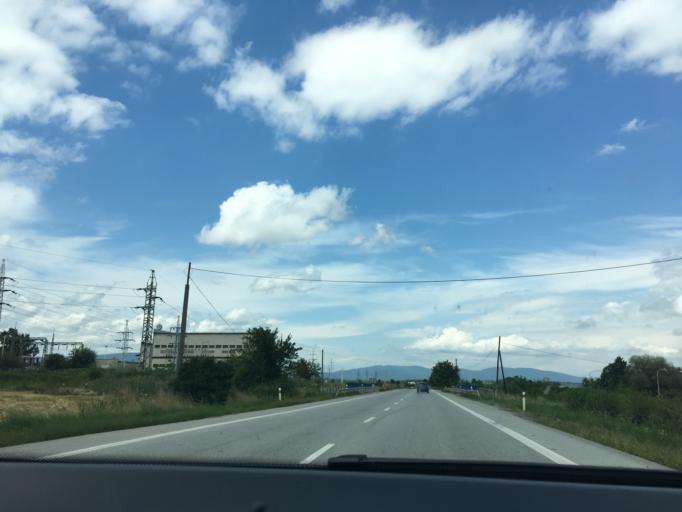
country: SK
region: Kosicky
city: Trebisov
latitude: 48.6297
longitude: 21.6939
